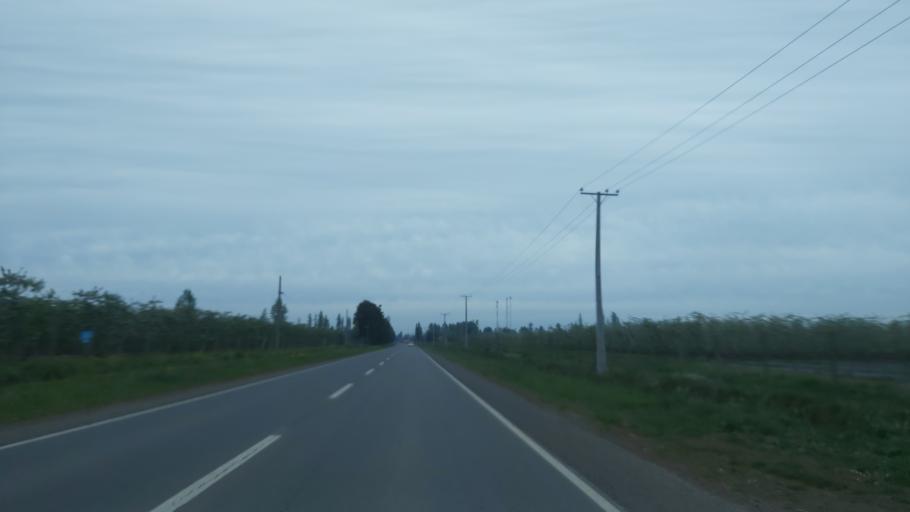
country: CL
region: Maule
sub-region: Provincia de Linares
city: Colbun
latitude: -35.7231
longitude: -71.4852
